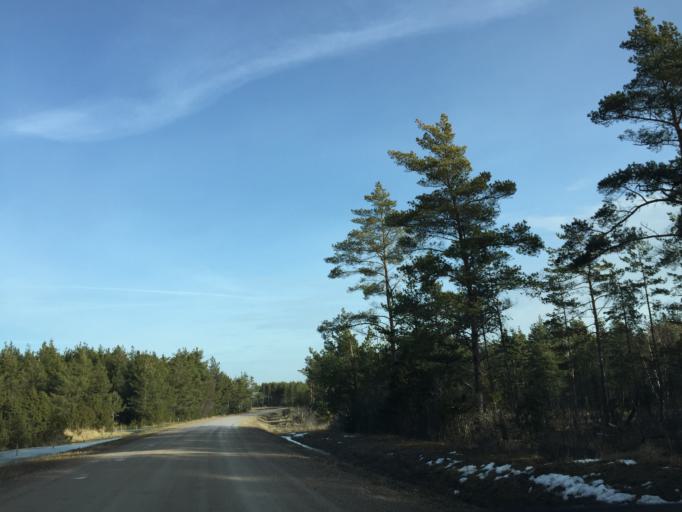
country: EE
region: Saare
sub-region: Kuressaare linn
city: Kuressaare
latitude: 58.2810
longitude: 21.9183
